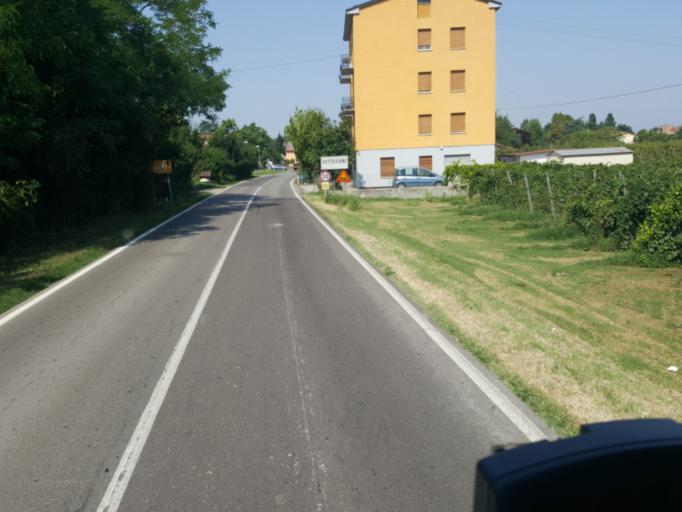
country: IT
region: Emilia-Romagna
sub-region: Provincia di Modena
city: Ca' di Sola
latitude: 44.5413
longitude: 10.9601
